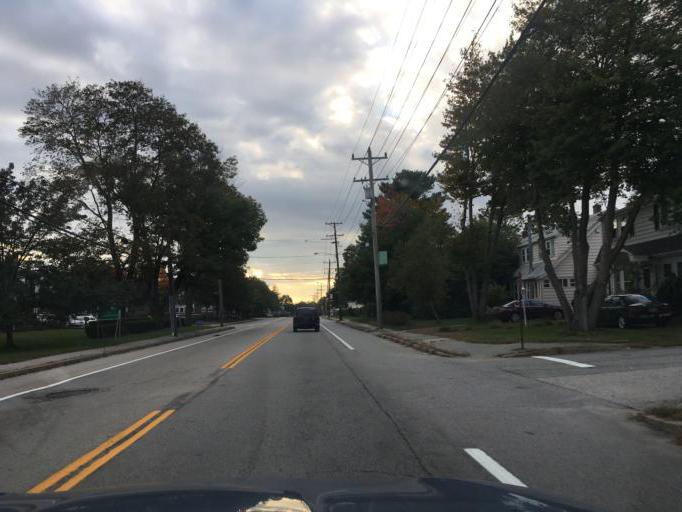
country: US
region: Rhode Island
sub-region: Kent County
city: Warwick
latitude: 41.7000
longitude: -71.4451
